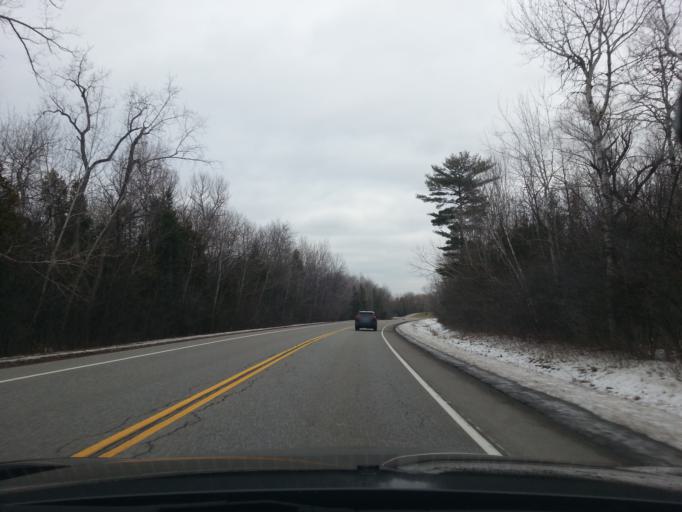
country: CA
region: Quebec
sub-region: Outaouais
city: Gatineau
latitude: 45.4635
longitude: -75.6097
